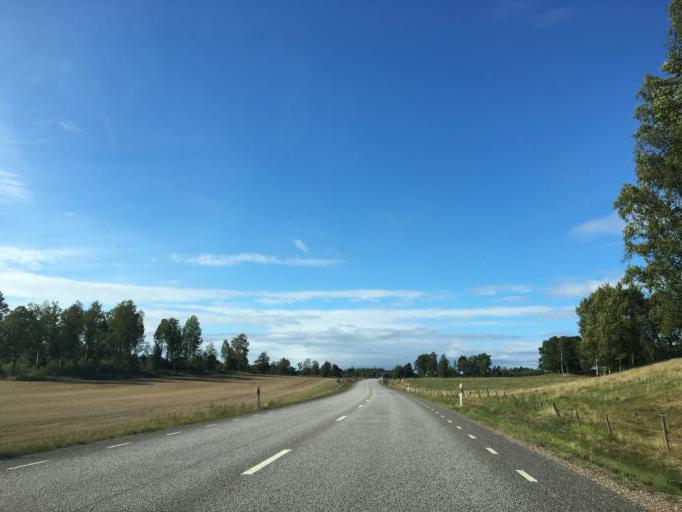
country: SE
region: Soedermanland
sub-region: Nykopings Kommun
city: Nykoping
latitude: 58.8153
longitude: 16.9417
